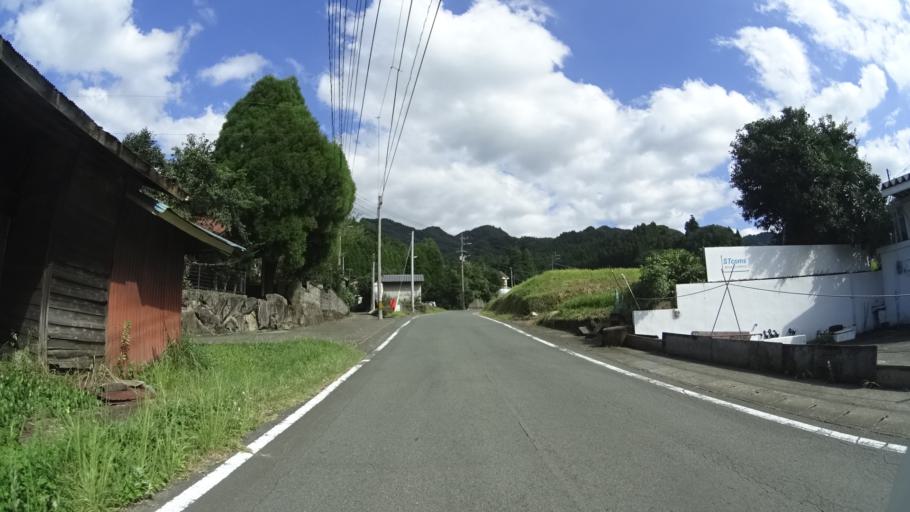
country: JP
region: Kumamoto
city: Aso
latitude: 32.8168
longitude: 131.1297
